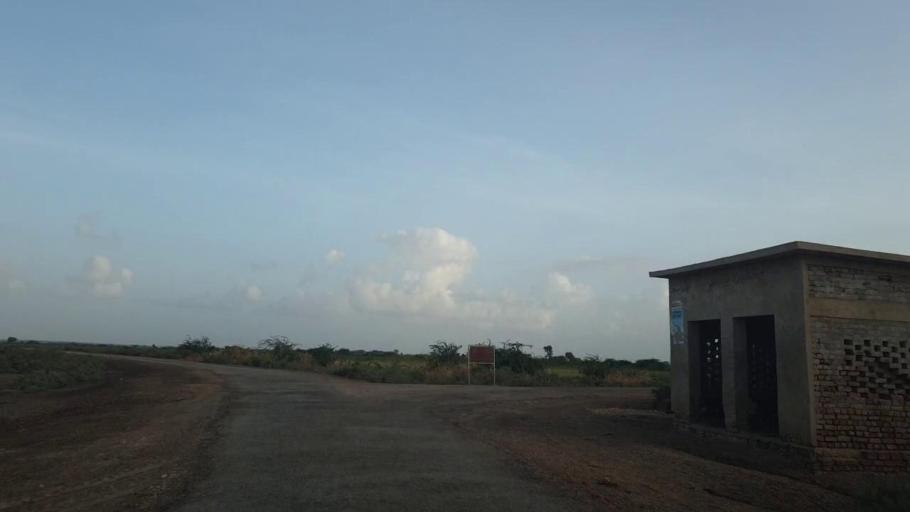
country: PK
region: Sindh
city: Kadhan
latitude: 24.5703
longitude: 69.1176
